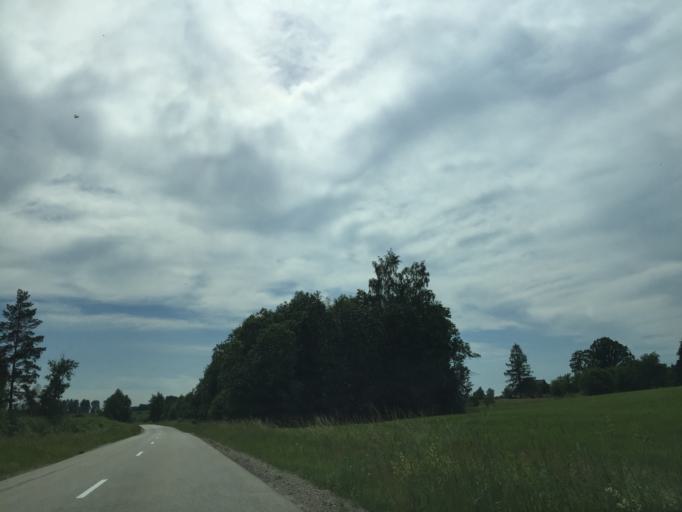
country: LV
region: Engure
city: Smarde
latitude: 57.0406
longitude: 23.2565
